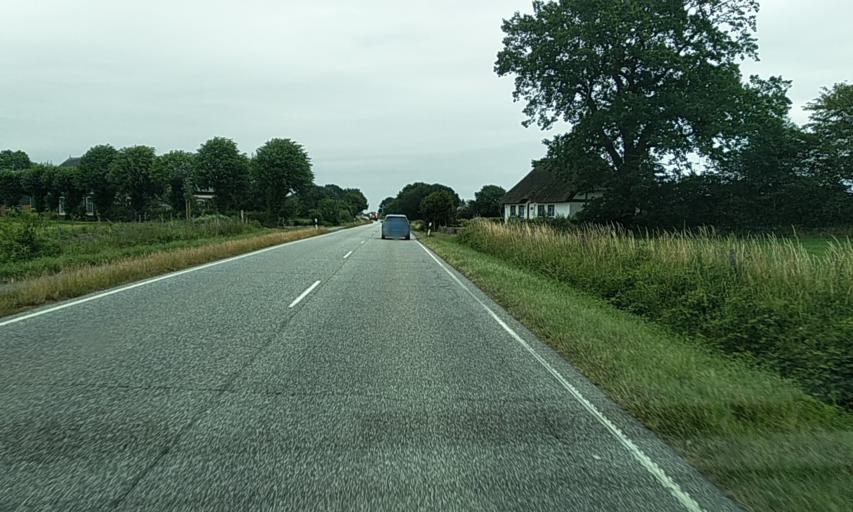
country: DE
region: Schleswig-Holstein
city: Grodersby
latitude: 54.6528
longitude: 9.8899
